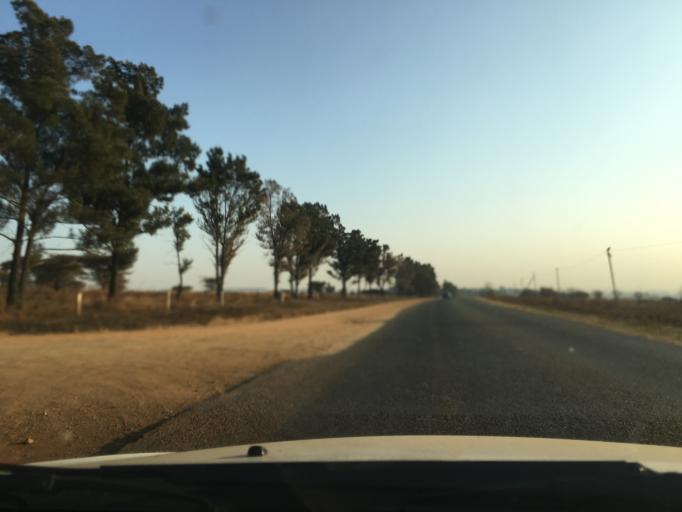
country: ZA
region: Gauteng
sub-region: West Rand District Municipality
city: Muldersdriseloop
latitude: -25.9989
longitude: 27.8574
